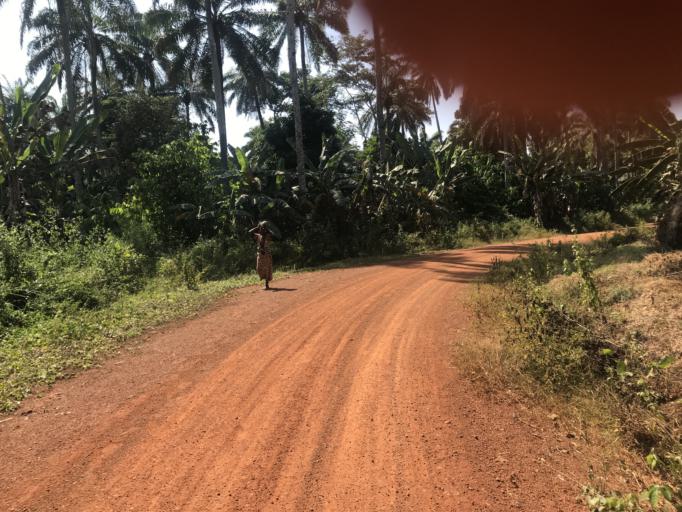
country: NG
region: Osun
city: Ikirun
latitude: 7.9320
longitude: 4.6295
